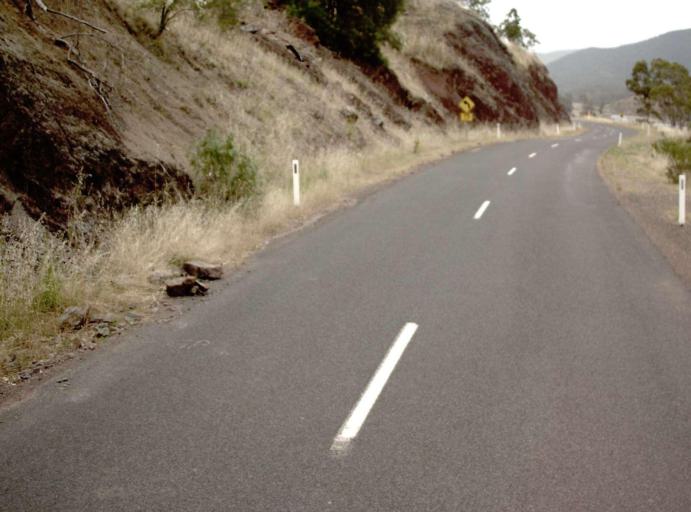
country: AU
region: Victoria
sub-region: Wellington
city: Heyfield
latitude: -37.6644
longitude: 146.6460
